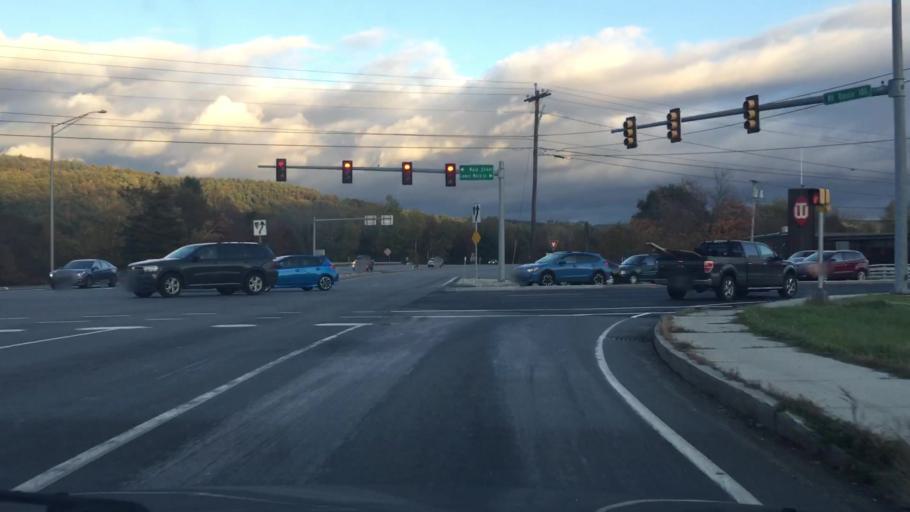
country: US
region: New Hampshire
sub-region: Cheshire County
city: Keene
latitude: 42.9214
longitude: -72.2762
